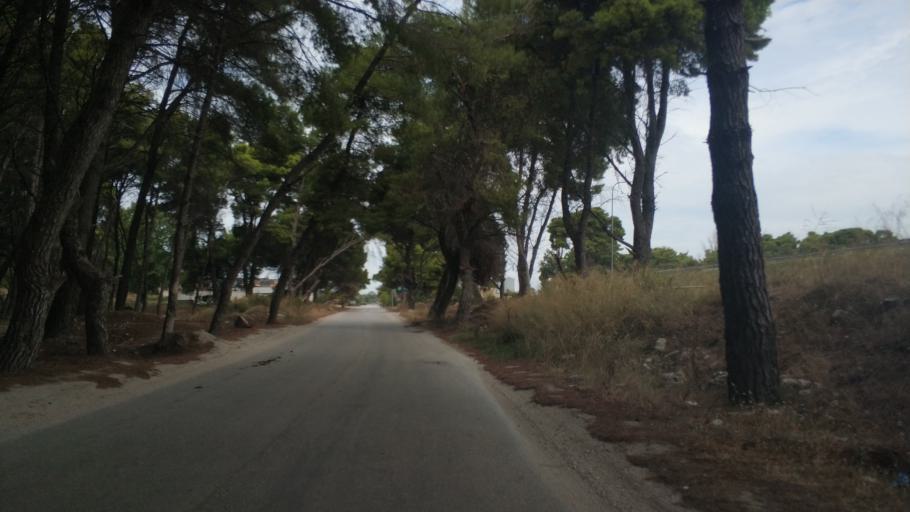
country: AL
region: Vlore
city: Vlore
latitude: 40.4701
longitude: 19.4595
